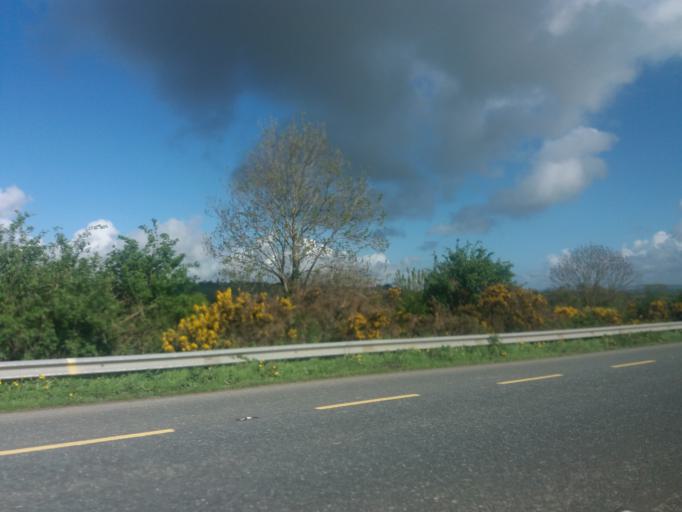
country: IE
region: Leinster
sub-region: Loch Garman
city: Enniscorthy
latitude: 52.5319
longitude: -6.5556
